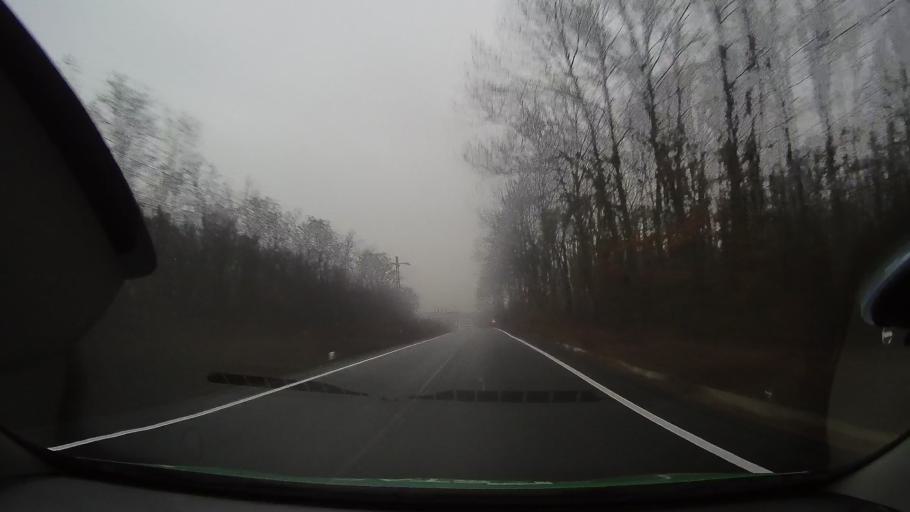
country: RO
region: Bihor
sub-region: Comuna Olcea
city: Olcea
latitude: 46.6963
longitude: 21.9648
